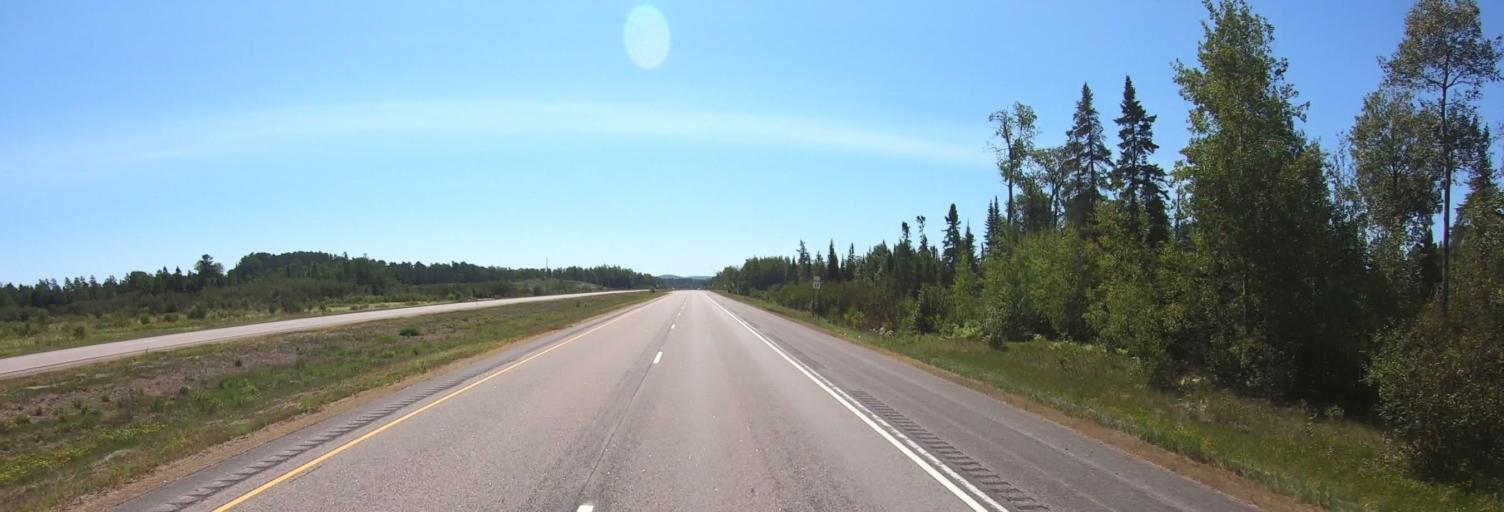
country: US
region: Minnesota
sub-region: Saint Louis County
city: Parkville
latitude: 47.6456
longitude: -92.5660
